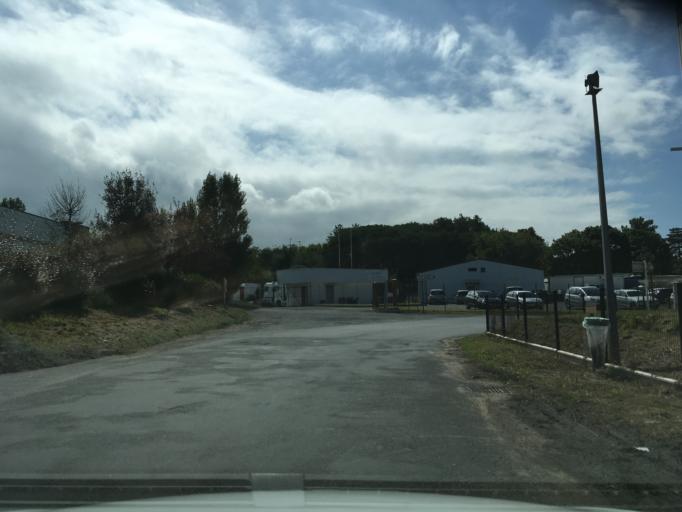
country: FR
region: Aquitaine
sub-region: Departement des Pyrenees-Atlantiques
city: Bayonne
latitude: 43.4904
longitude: -1.4574
